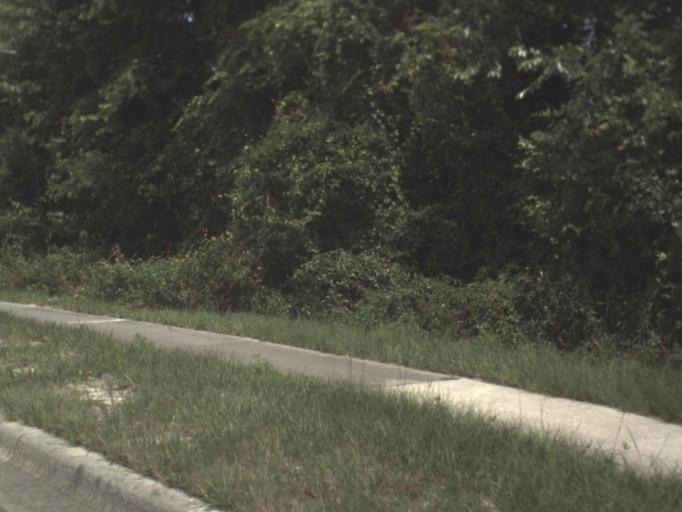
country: US
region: Florida
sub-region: Alachua County
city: Alachua
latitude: 29.6604
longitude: -82.4314
